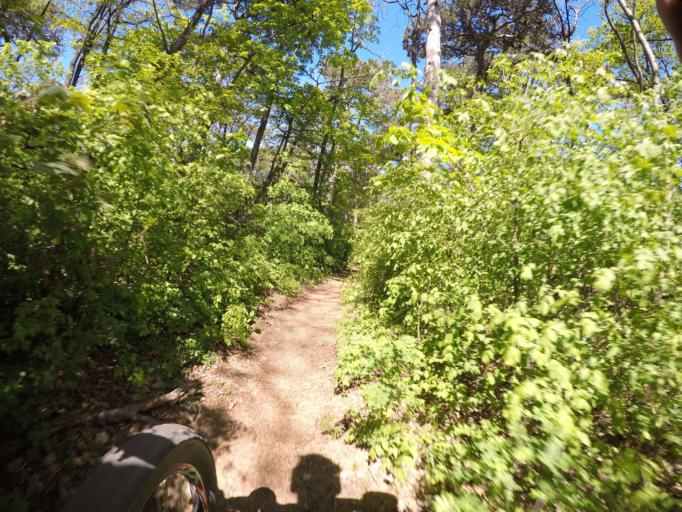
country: AT
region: Lower Austria
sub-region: Politischer Bezirk Modling
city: Gumpoldskirchen
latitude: 48.0631
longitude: 16.2808
